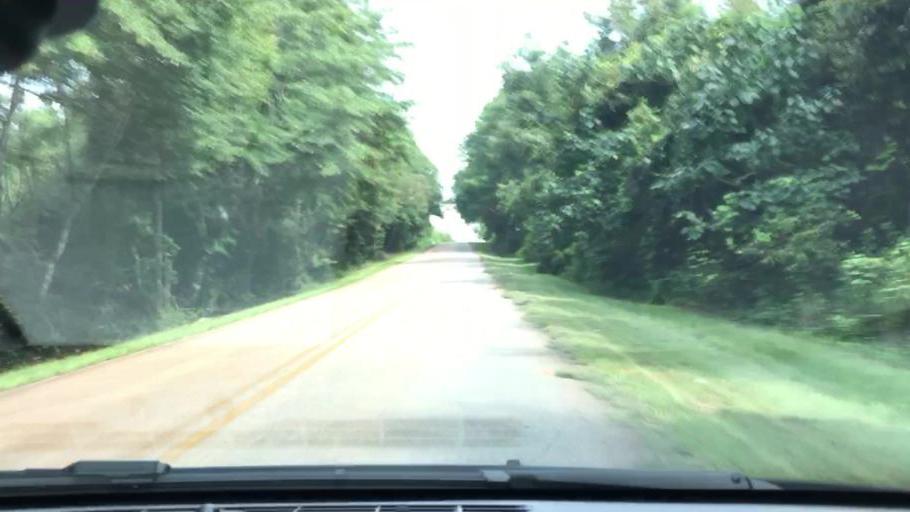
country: US
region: Georgia
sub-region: Clay County
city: Fort Gaines
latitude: 31.5698
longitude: -84.9979
